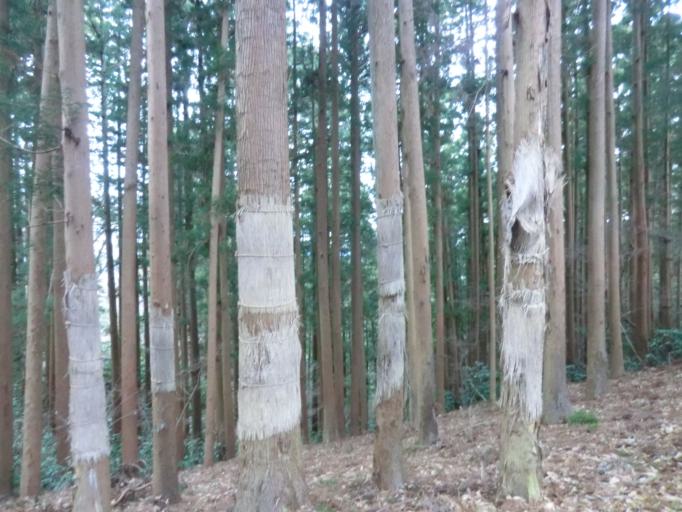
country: JP
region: Tokyo
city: Hachioji
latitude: 35.6258
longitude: 139.2434
